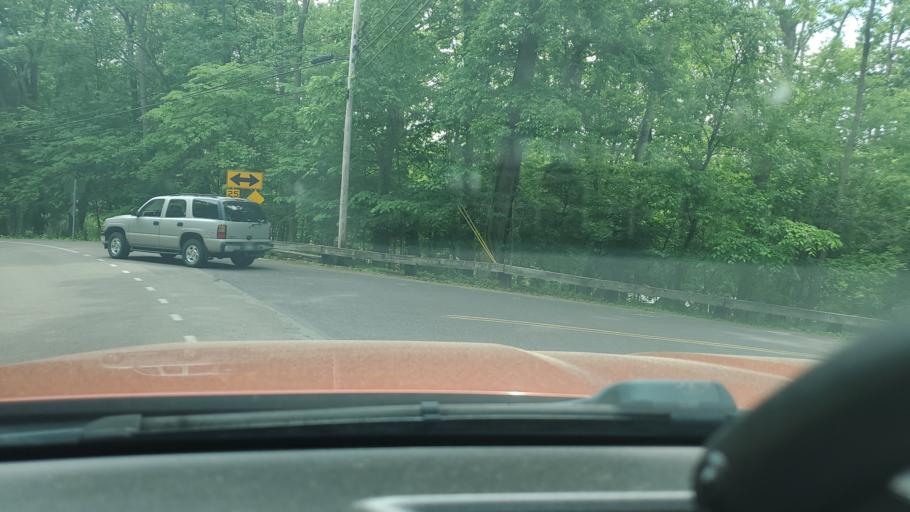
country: US
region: Pennsylvania
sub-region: Montgomery County
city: Red Hill
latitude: 40.3388
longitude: -75.4765
